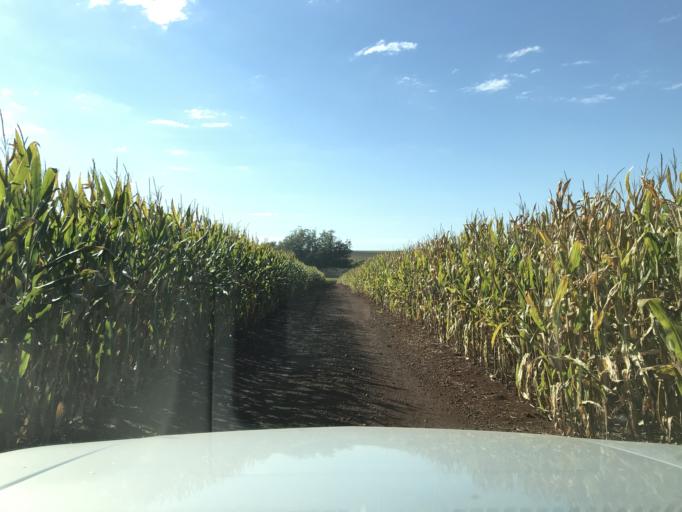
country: BR
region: Parana
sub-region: Palotina
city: Palotina
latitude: -24.2639
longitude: -53.8080
